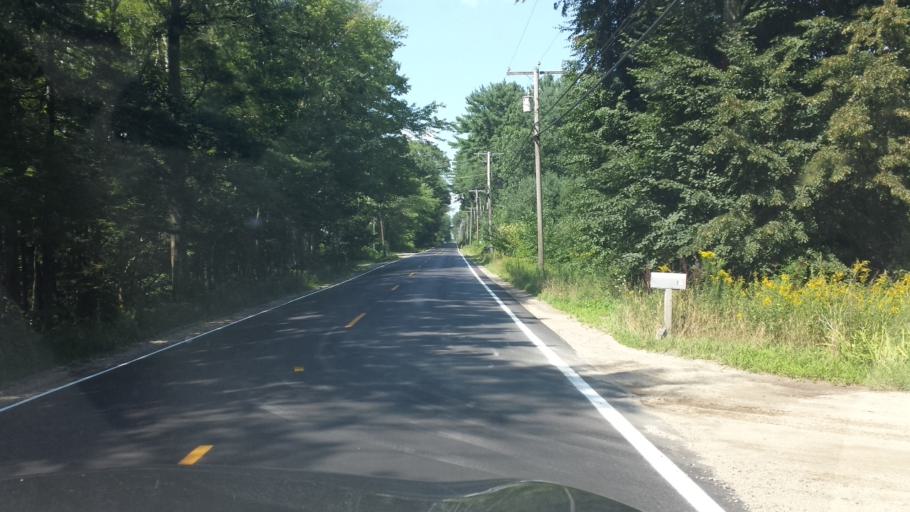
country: US
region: Maine
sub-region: York County
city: Arundel
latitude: 43.3924
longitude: -70.4826
